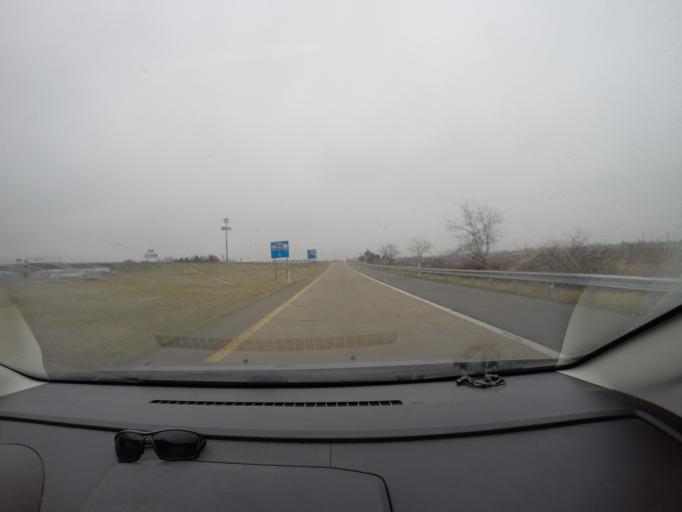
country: US
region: Tennessee
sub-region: Rutherford County
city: Plainview
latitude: 35.7230
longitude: -86.3223
